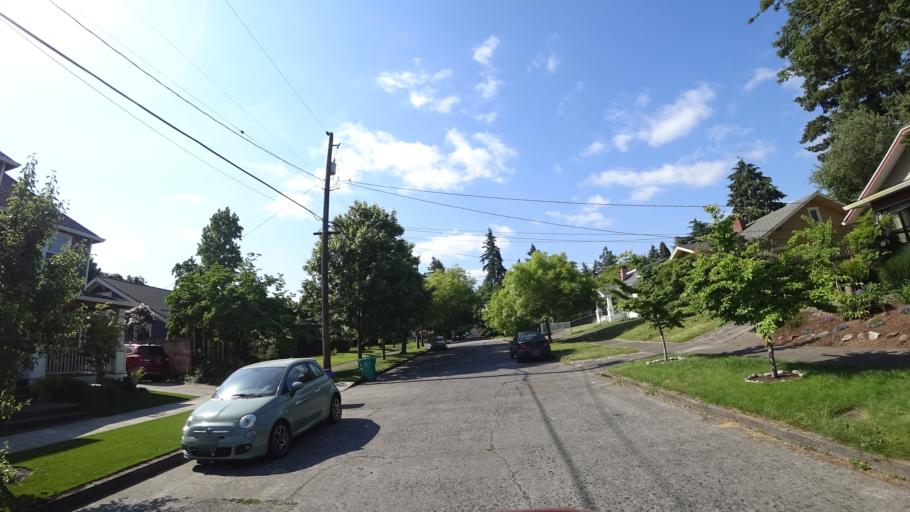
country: US
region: Oregon
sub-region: Multnomah County
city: Portland
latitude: 45.5696
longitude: -122.6435
